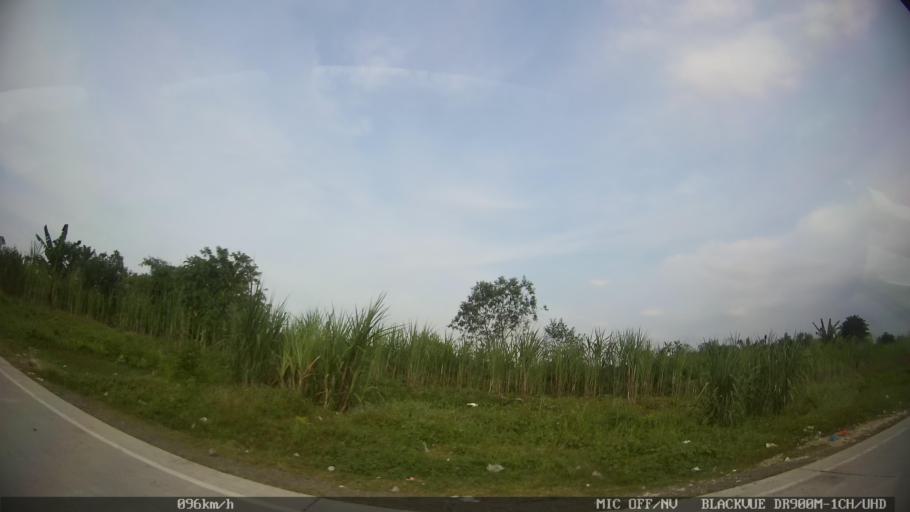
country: ID
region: North Sumatra
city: Binjai
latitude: 3.5978
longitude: 98.5329
